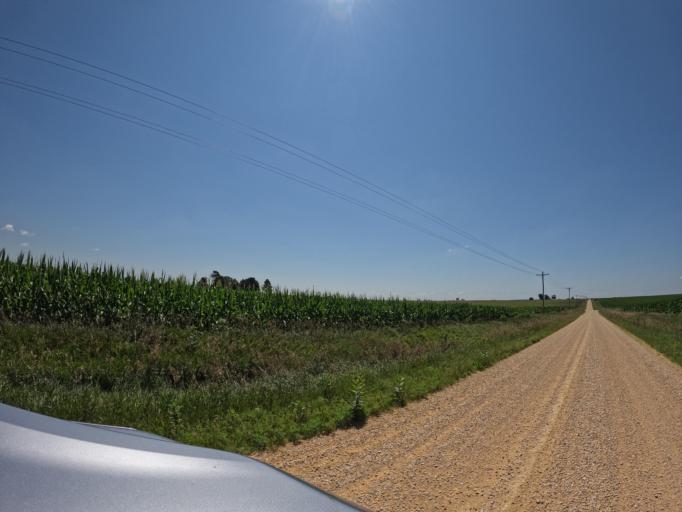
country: US
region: Iowa
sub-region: Clinton County
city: Camanche
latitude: 41.7807
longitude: -90.3936
